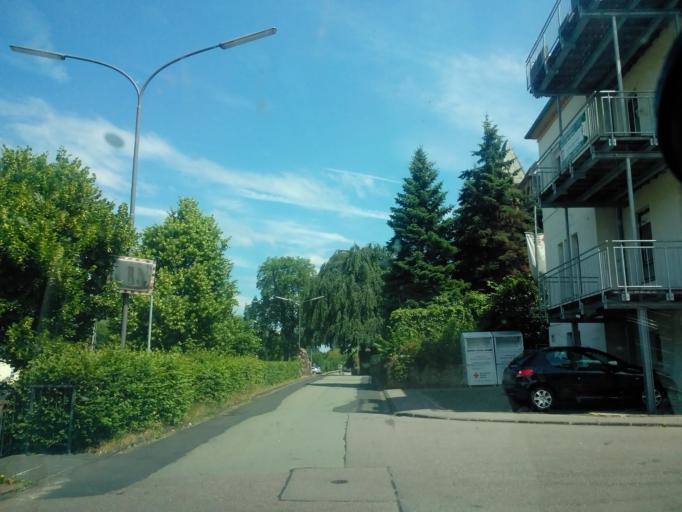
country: DE
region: Rheinland-Pfalz
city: Saarburg
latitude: 49.6063
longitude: 6.5576
